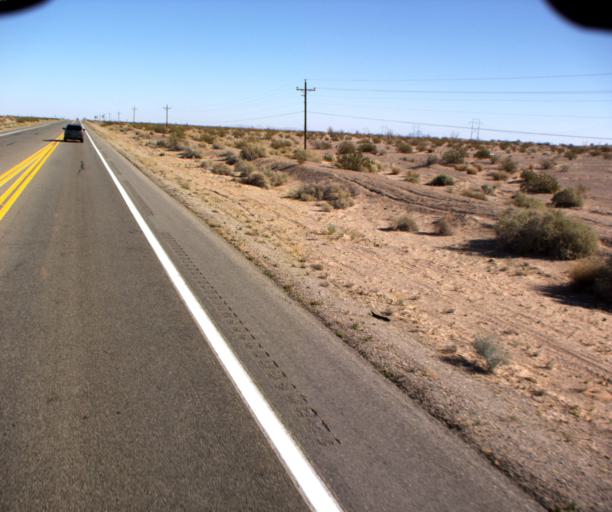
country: US
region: Arizona
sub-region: Yuma County
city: Fortuna Foothills
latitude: 32.8098
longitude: -114.3798
